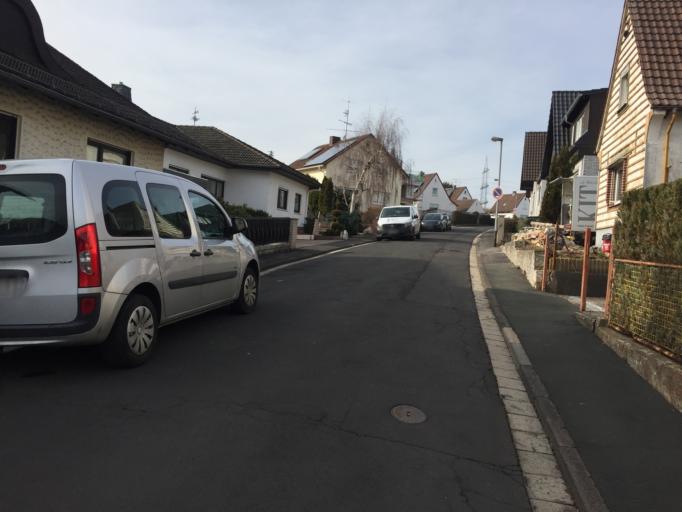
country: DE
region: Hesse
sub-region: Regierungsbezirk Giessen
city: Fronhausen
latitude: 50.6794
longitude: 8.6999
